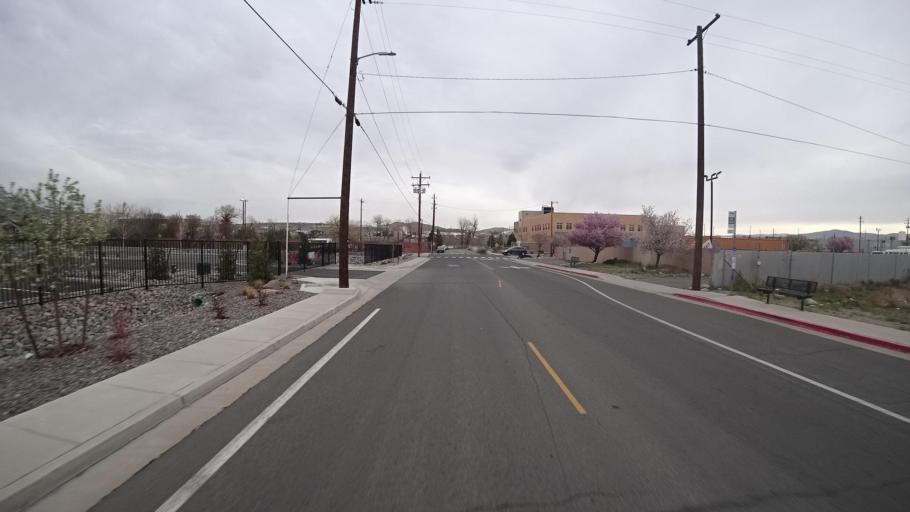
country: US
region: Nevada
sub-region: Washoe County
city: Reno
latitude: 39.5289
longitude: -119.7921
